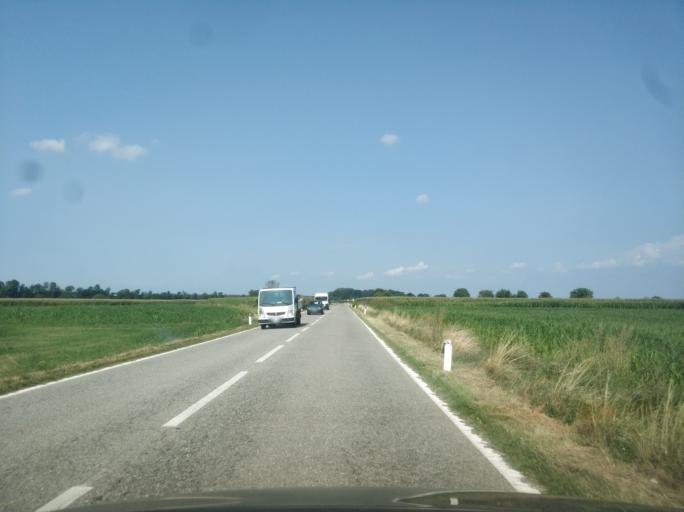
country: IT
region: Piedmont
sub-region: Provincia di Cuneo
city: Caraglio
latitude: 44.4386
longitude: 7.4494
